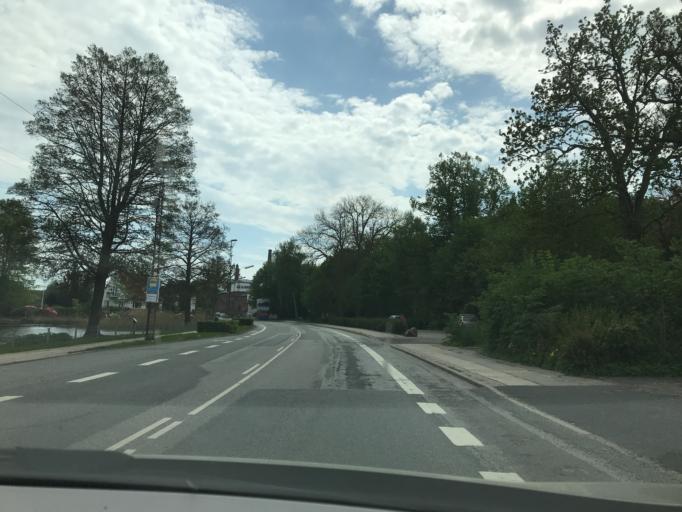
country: DK
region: South Denmark
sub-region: Assens Kommune
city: Assens
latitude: 55.2666
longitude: 9.9020
